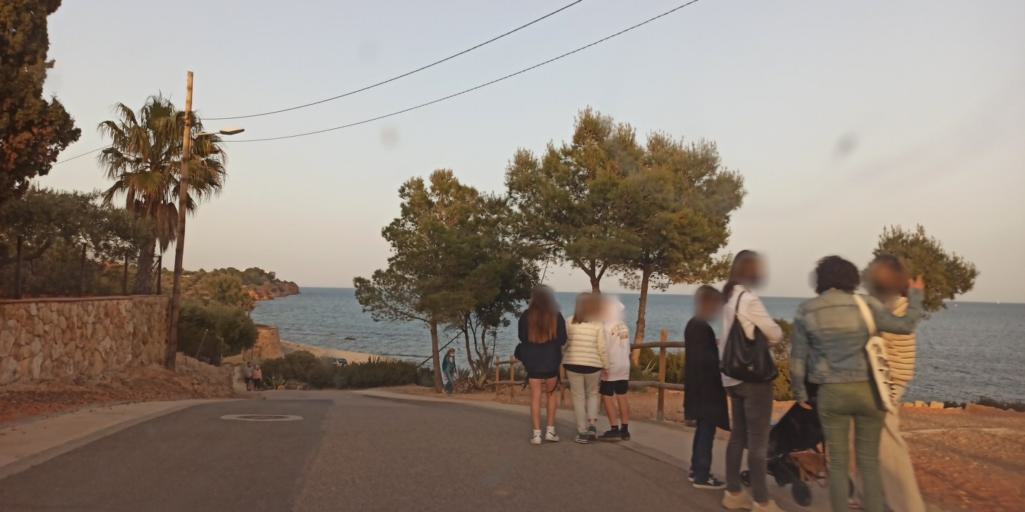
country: ES
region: Catalonia
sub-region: Provincia de Tarragona
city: L'Ampolla
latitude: 40.8144
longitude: 0.7195
